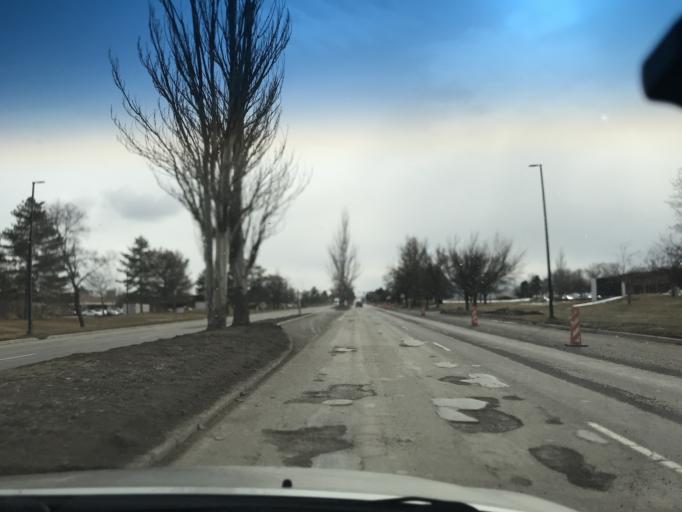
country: US
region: Utah
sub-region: Salt Lake County
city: West Valley City
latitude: 40.7786
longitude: -112.0251
